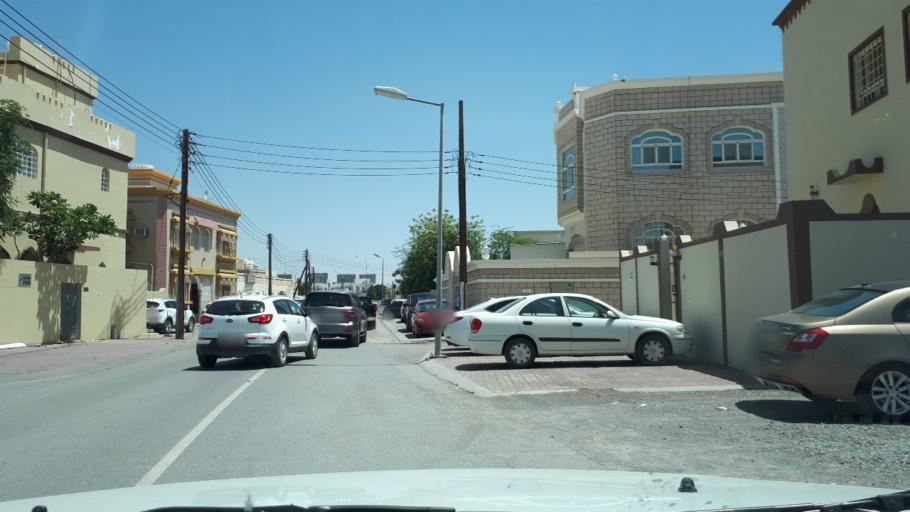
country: OM
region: Muhafazat ad Dakhiliyah
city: Nizwa
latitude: 22.8801
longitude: 57.5315
